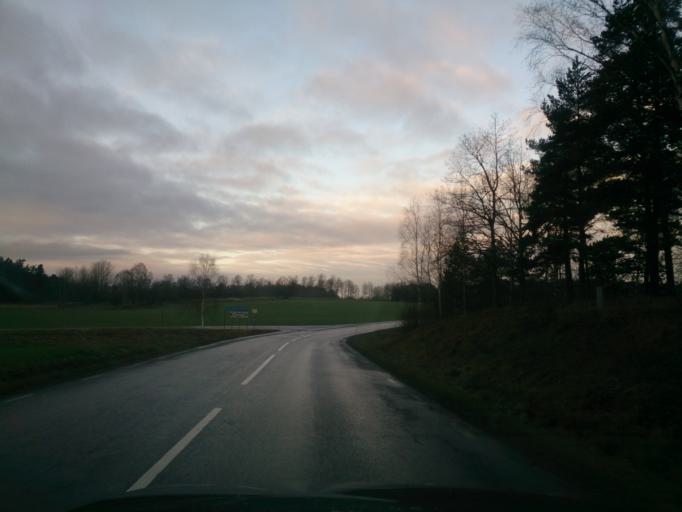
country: SE
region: OEstergoetland
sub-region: Norrkopings Kommun
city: Kimstad
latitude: 58.3972
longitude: 15.9543
